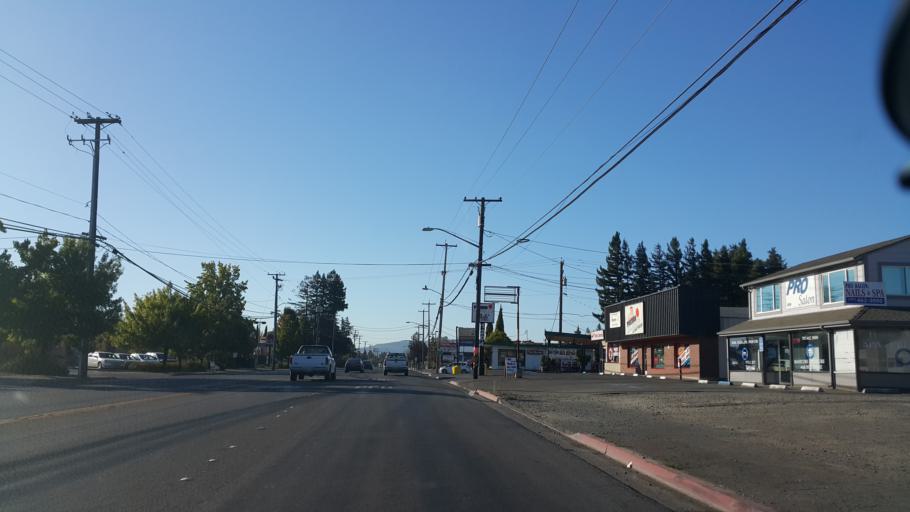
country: US
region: California
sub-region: Mendocino County
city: Ukiah
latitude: 39.1670
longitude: -123.2112
